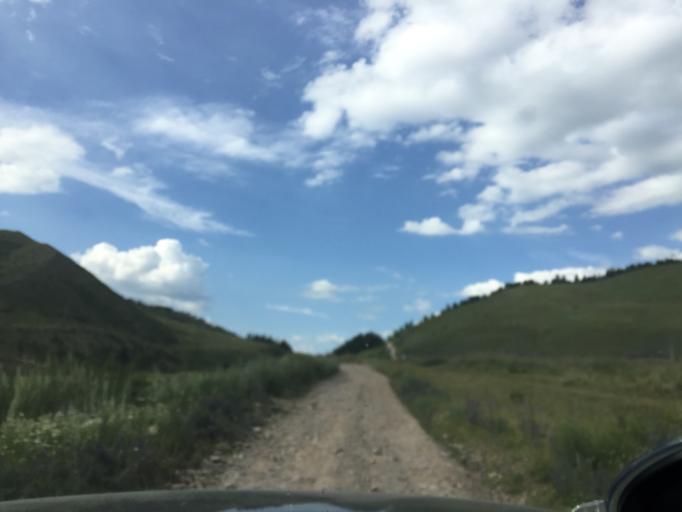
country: KG
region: Ysyk-Koel
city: Teploklyuchenka
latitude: 42.6741
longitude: 78.9010
